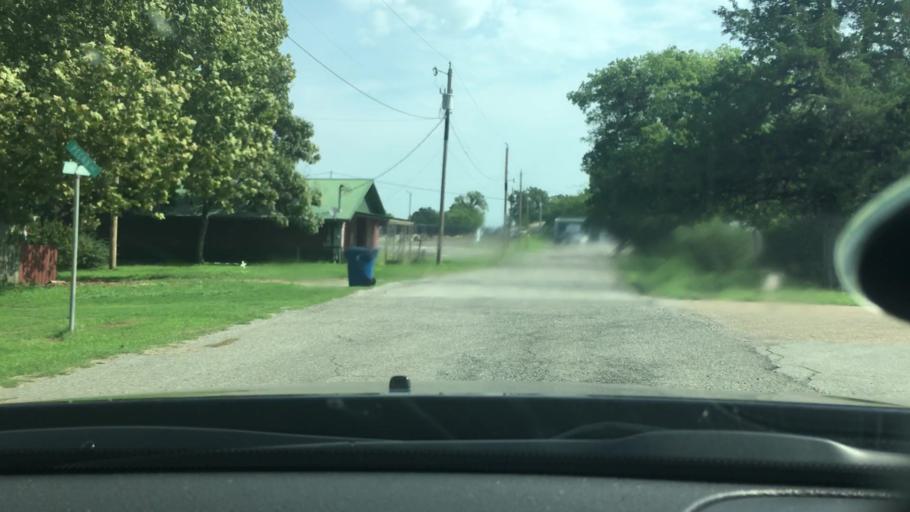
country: US
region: Oklahoma
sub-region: Atoka County
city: Atoka
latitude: 34.4682
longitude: -96.0537
